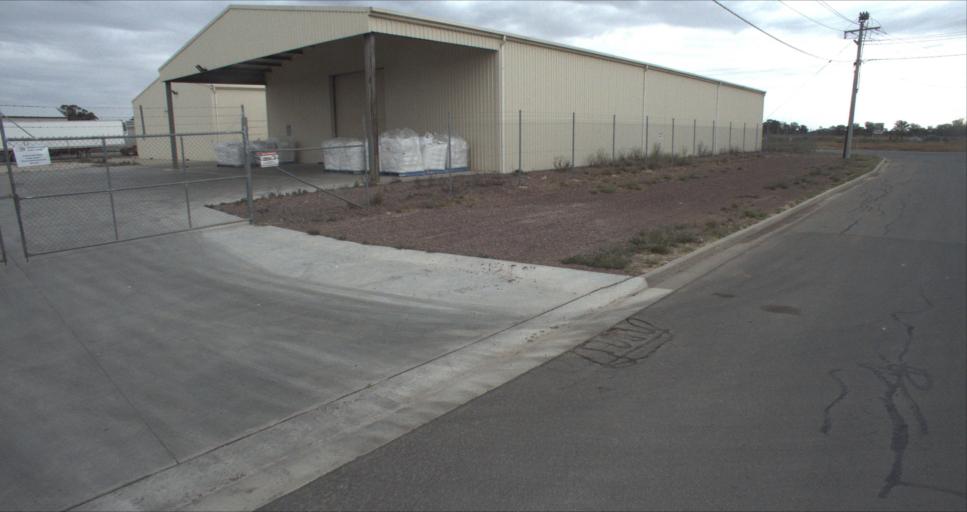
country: AU
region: New South Wales
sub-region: Leeton
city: Leeton
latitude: -34.5458
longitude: 146.3870
